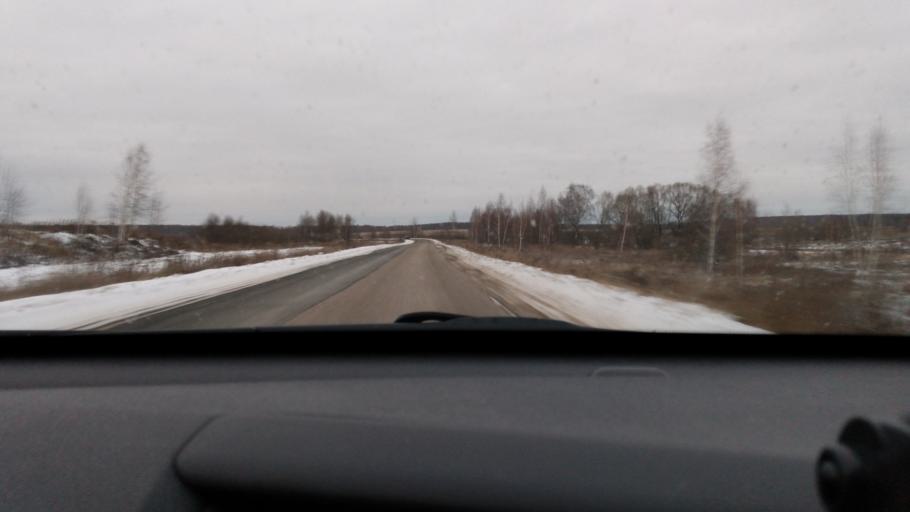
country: RU
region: Moskovskaya
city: Meshcherino
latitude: 55.3003
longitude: 38.3439
